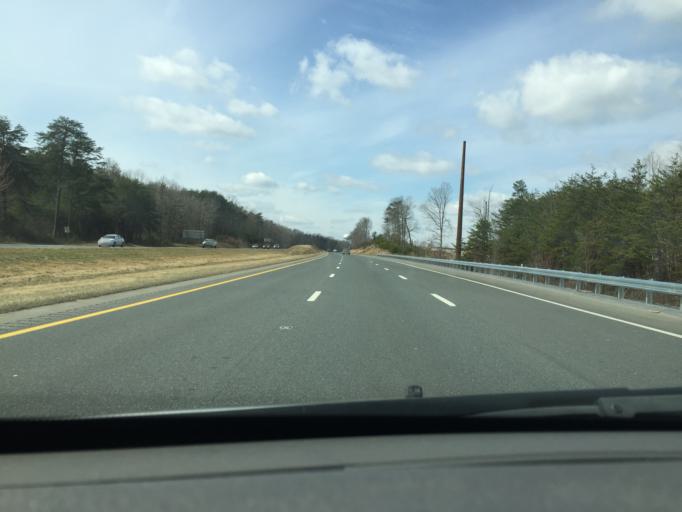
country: US
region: Virginia
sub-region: Campbell County
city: Timberlake
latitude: 37.3120
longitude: -79.2421
